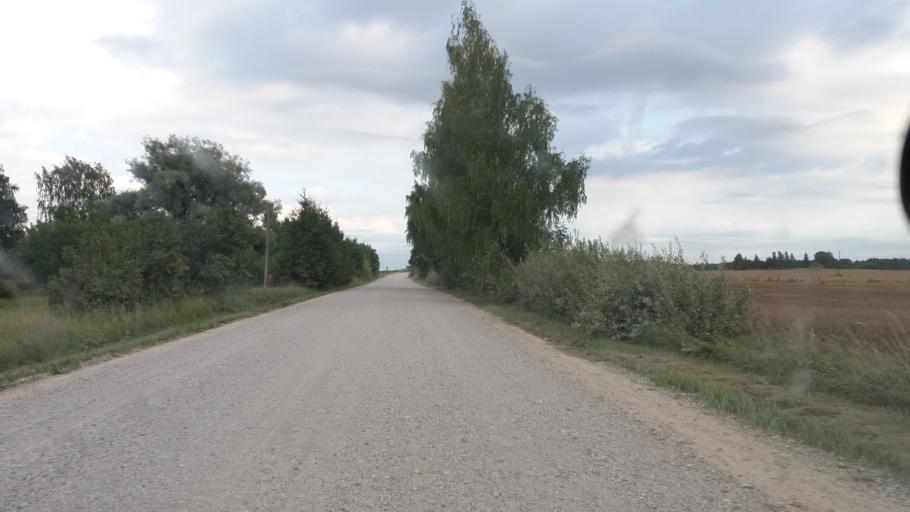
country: LV
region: Talsu Rajons
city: Sabile
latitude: 57.0338
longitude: 22.5743
